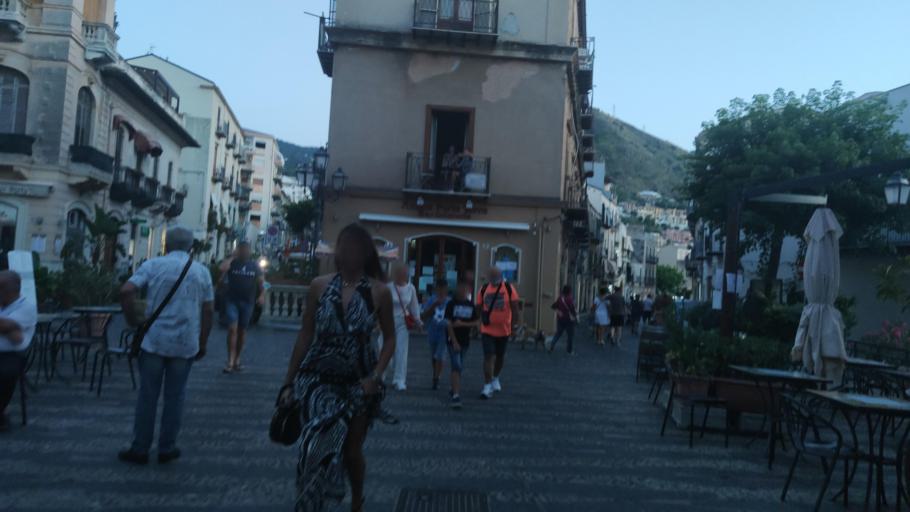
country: IT
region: Sicily
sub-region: Palermo
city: Cefalu
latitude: 38.0369
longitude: 14.0219
